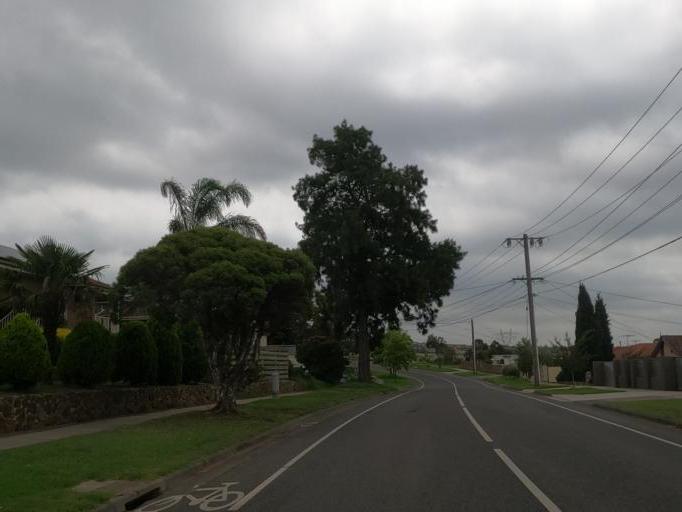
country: AU
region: Victoria
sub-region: Hume
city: Broadmeadows
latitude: -37.6695
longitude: 144.9093
